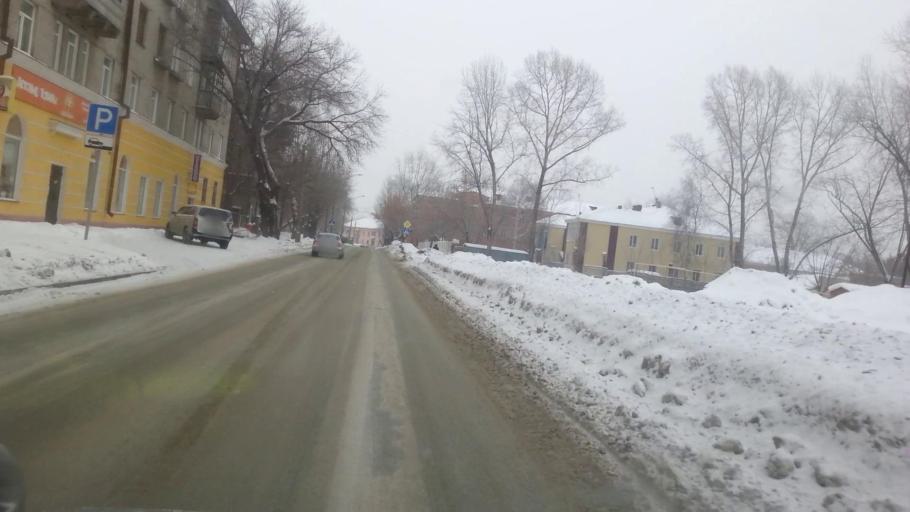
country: RU
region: Altai Krai
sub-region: Gorod Barnaulskiy
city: Barnaul
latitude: 53.3793
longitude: 83.7253
